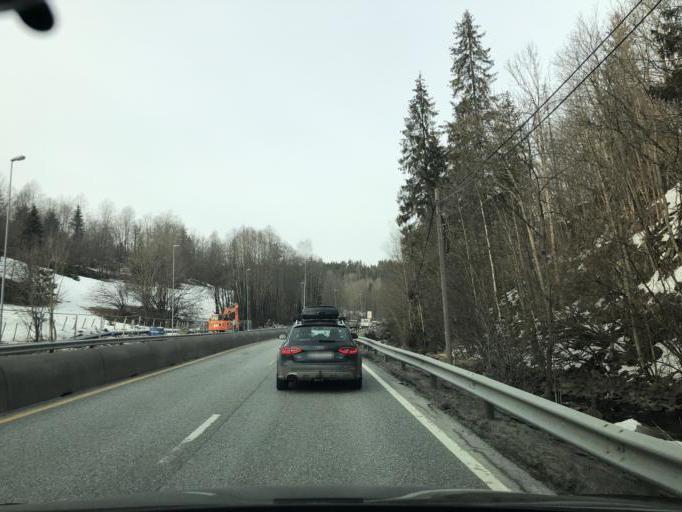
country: NO
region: Akershus
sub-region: Baerum
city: Skui
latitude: 59.9422
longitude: 10.4043
